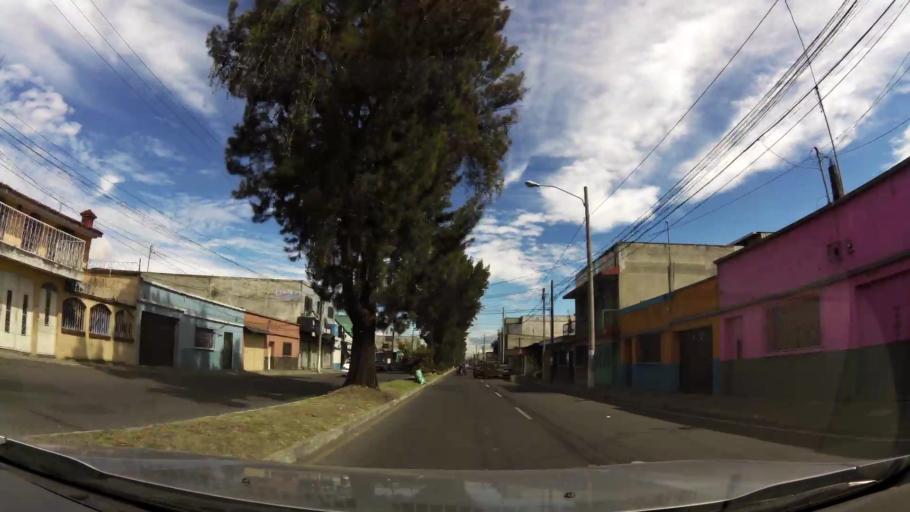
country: GT
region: Guatemala
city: Mixco
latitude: 14.6557
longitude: -90.5838
